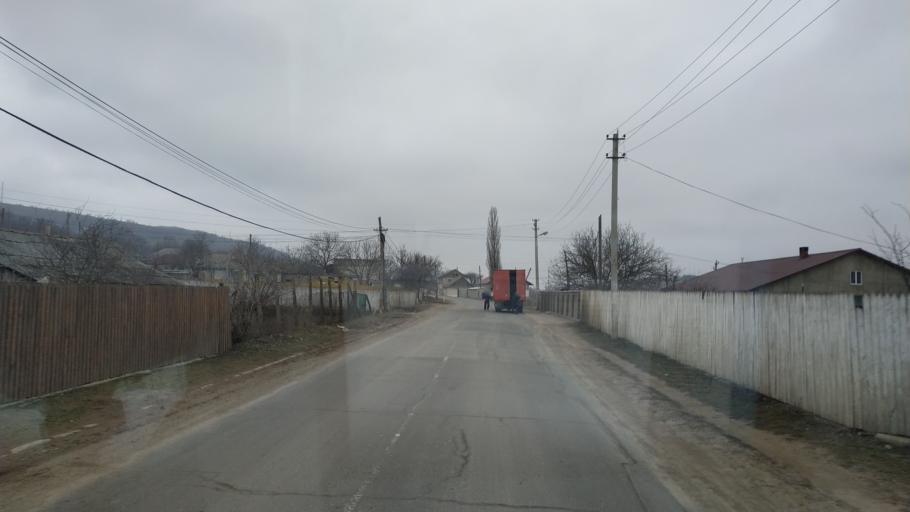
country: MD
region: Stinga Nistrului
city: Bucovat
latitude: 46.9834
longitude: 28.4493
